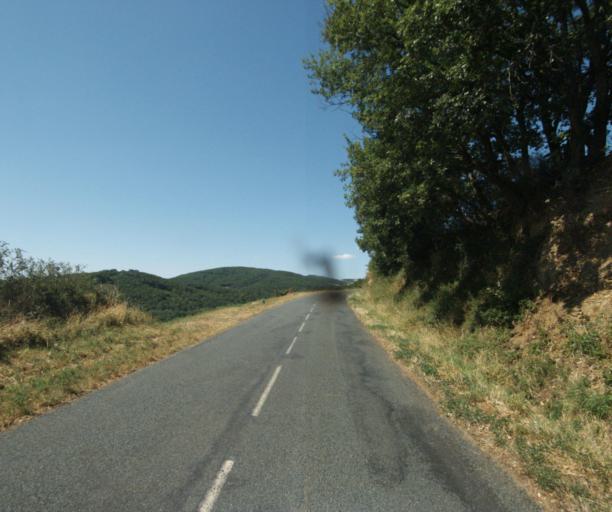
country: FR
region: Rhone-Alpes
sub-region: Departement du Rhone
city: Bessenay
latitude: 45.7928
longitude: 4.5384
